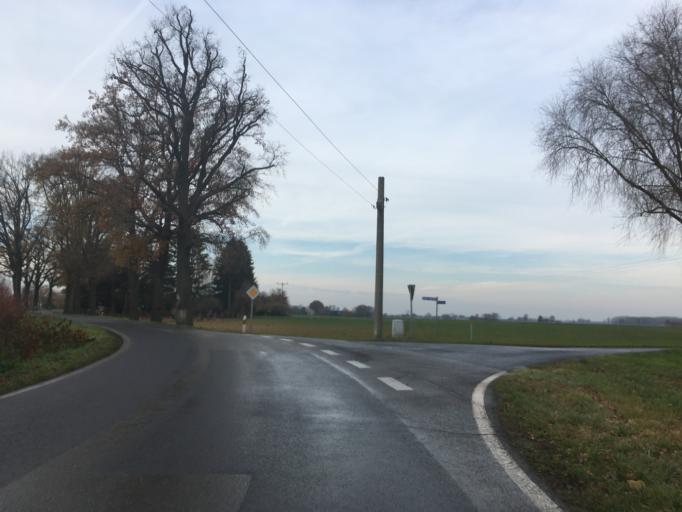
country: DE
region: Brandenburg
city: Letschin
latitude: 52.7038
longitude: 14.3504
